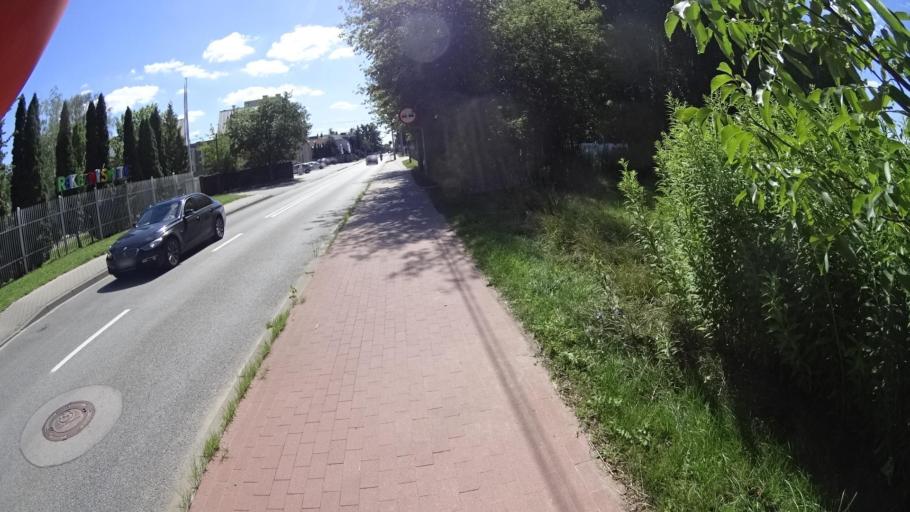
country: PL
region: Masovian Voivodeship
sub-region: Powiat piaseczynski
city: Jozefoslaw
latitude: 52.0870
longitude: 21.0469
